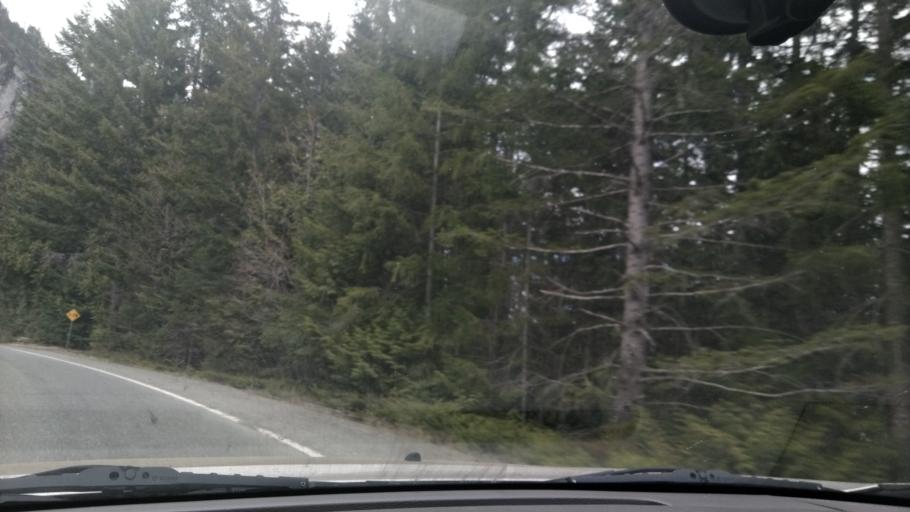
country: CA
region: British Columbia
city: Campbell River
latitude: 49.8469
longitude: -125.6427
